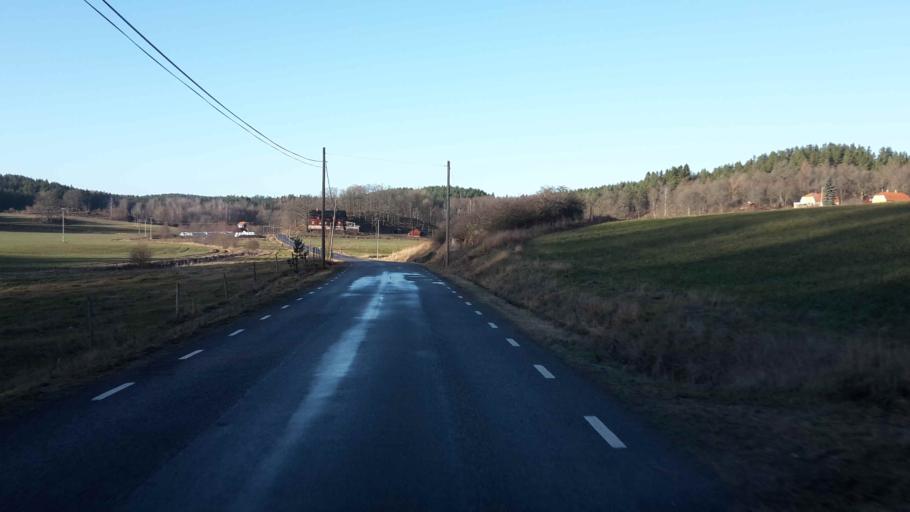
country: SE
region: Kalmar
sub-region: Vasterviks Kommun
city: Overum
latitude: 58.1509
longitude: 16.3149
